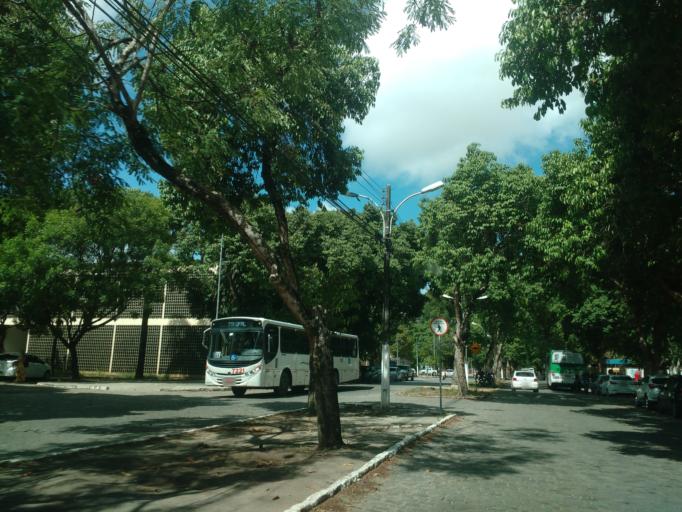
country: BR
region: Alagoas
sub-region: Satuba
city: Satuba
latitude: -9.5553
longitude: -35.7772
